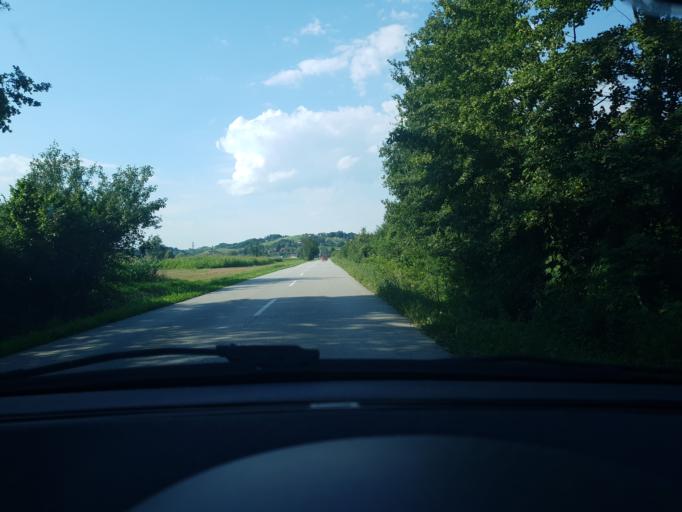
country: HR
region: Zagrebacka
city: Pojatno
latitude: 45.9432
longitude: 15.8122
